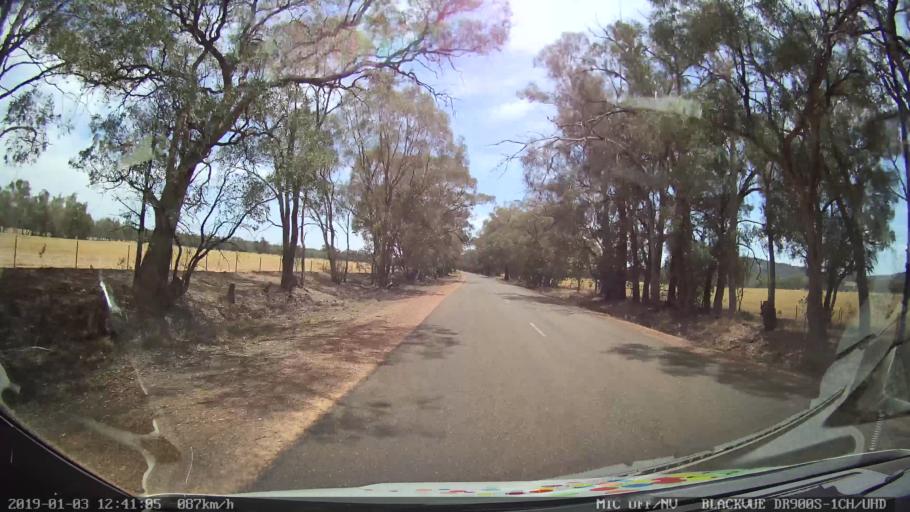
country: AU
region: New South Wales
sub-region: Weddin
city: Grenfell
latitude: -33.8043
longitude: 148.2144
